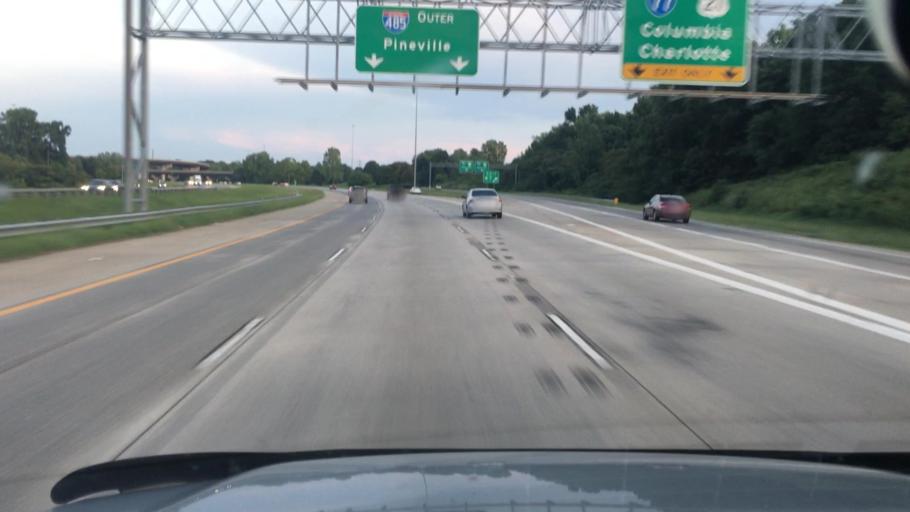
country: US
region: North Carolina
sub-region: Mecklenburg County
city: Pineville
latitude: 35.1304
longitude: -80.9229
